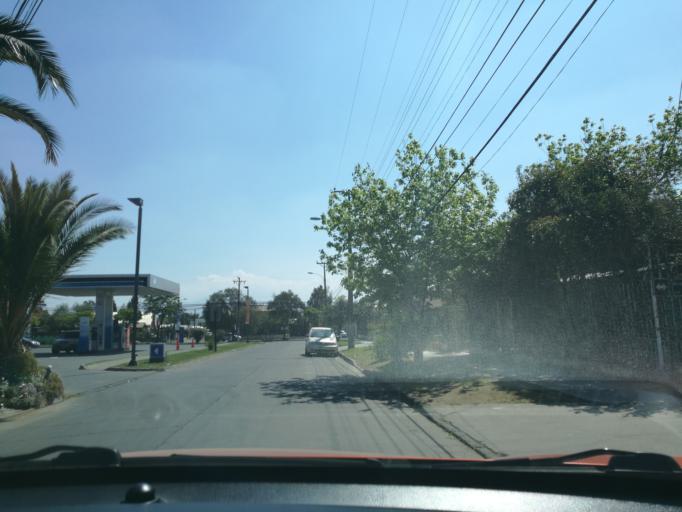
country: CL
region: O'Higgins
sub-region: Provincia de Cachapoal
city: Rancagua
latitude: -34.1625
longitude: -70.7383
